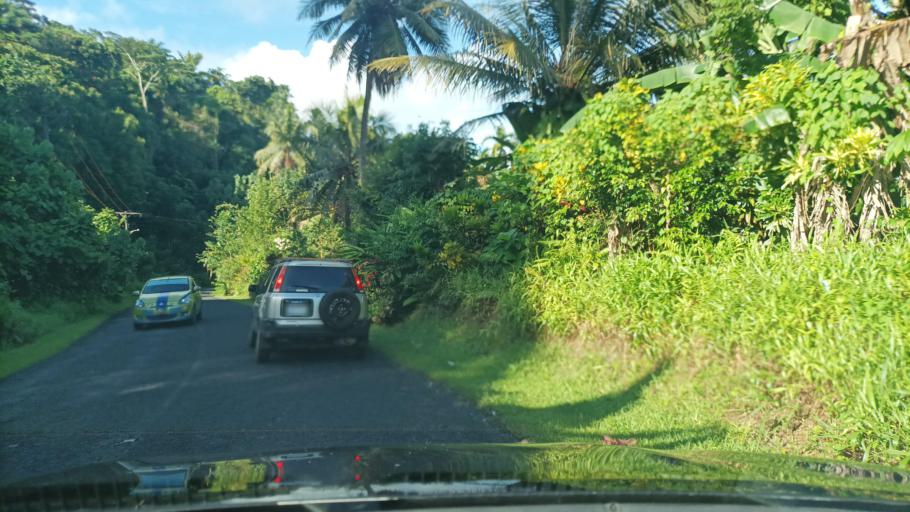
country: FM
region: Pohnpei
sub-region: Kolonia Municipality
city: Kolonia Town
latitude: 6.9485
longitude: 158.1874
